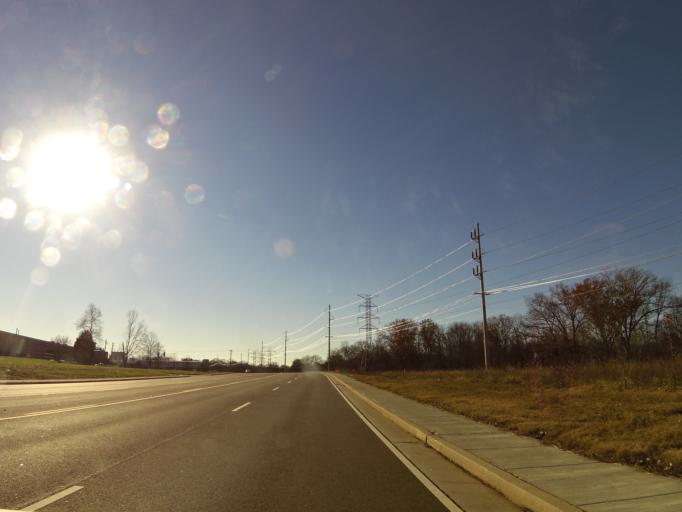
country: US
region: Tennessee
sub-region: Knox County
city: Knoxville
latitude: 36.0253
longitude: -84.0294
